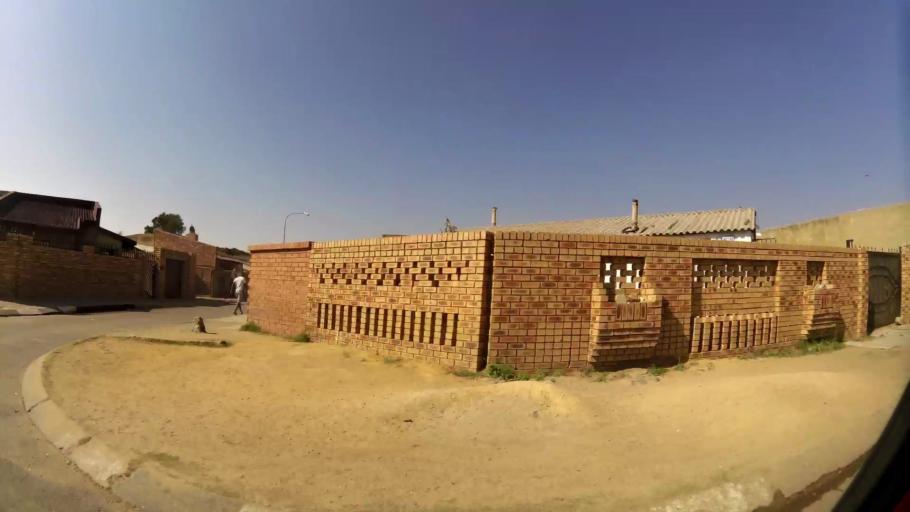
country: ZA
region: Gauteng
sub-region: City of Johannesburg Metropolitan Municipality
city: Soweto
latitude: -26.2418
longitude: 27.9534
